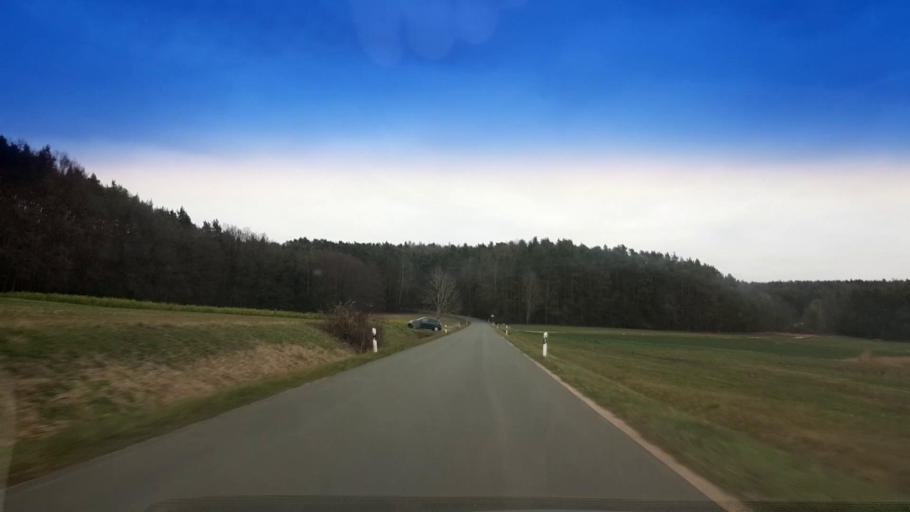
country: DE
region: Bavaria
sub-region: Upper Franconia
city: Pettstadt
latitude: 49.7739
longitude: 10.9161
